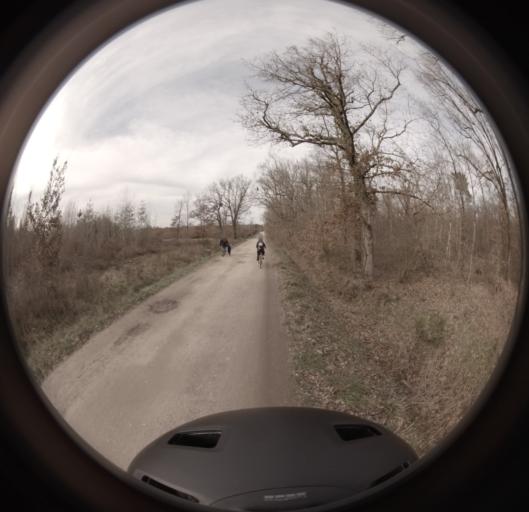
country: FR
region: Midi-Pyrenees
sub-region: Departement du Tarn-et-Garonne
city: Montech
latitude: 43.9632
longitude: 1.2669
